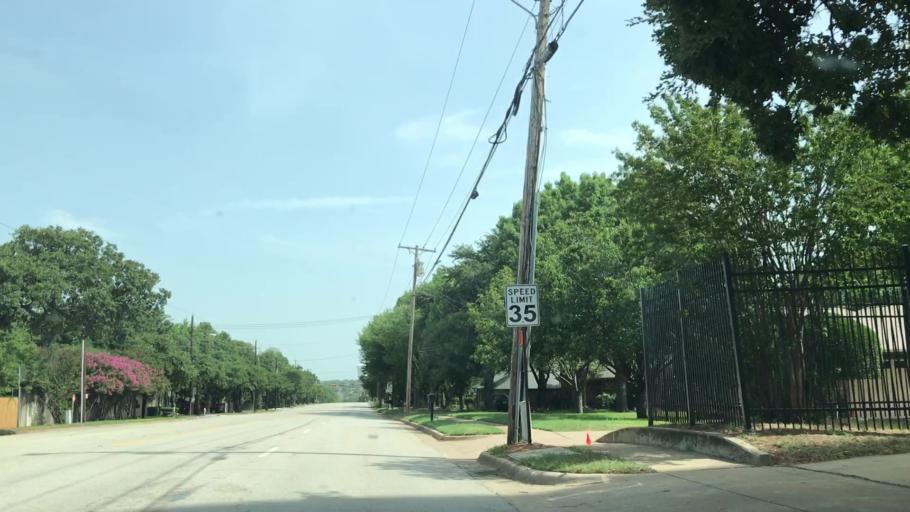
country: US
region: Texas
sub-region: Tarrant County
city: Euless
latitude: 32.8566
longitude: -97.0824
